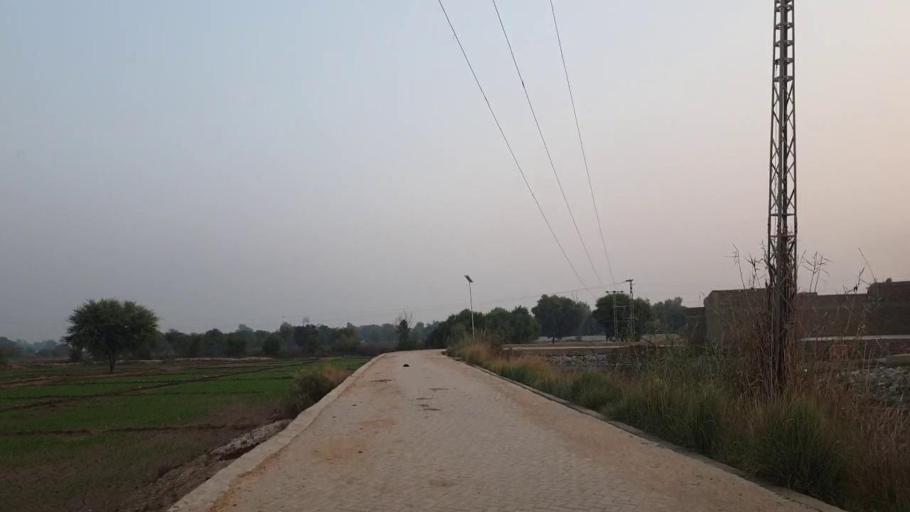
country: PK
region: Sindh
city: Bhan
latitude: 26.5216
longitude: 67.7115
